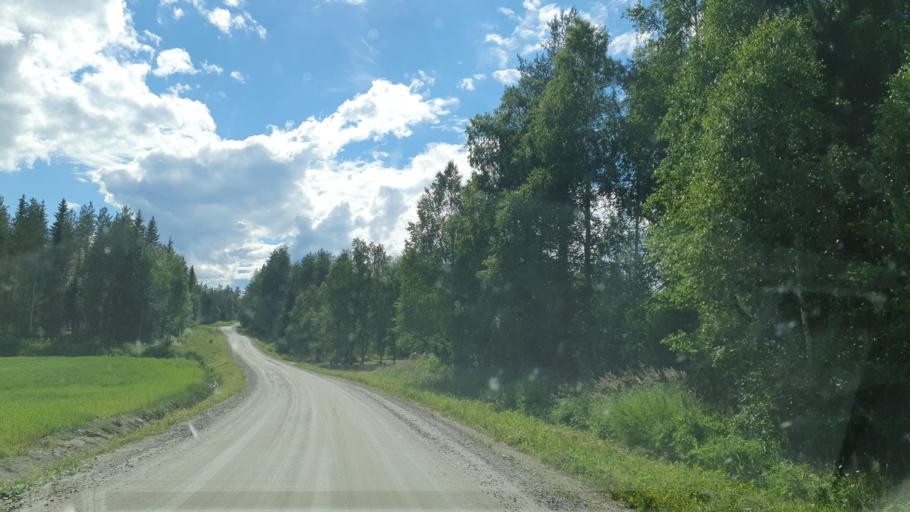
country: FI
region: Kainuu
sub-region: Kehys-Kainuu
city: Kuhmo
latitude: 64.1319
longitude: 29.6560
